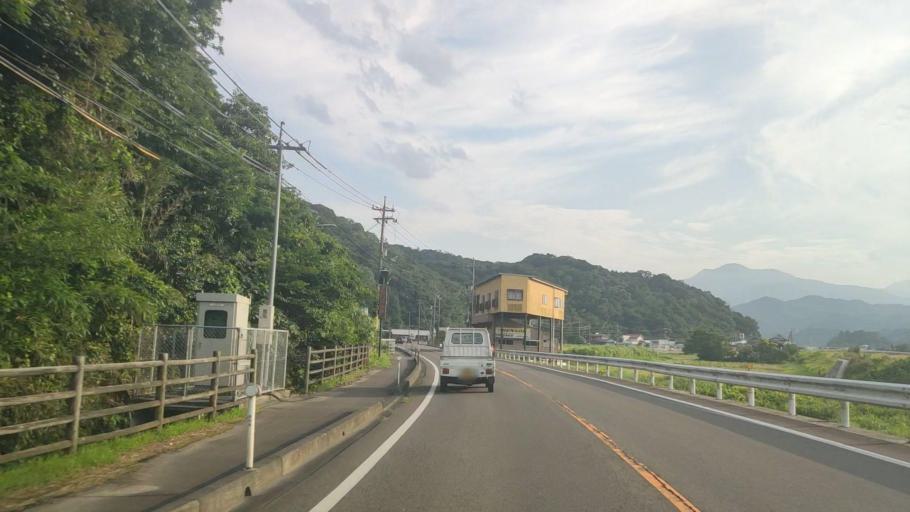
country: JP
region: Tottori
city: Kurayoshi
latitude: 35.3713
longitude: 133.7678
